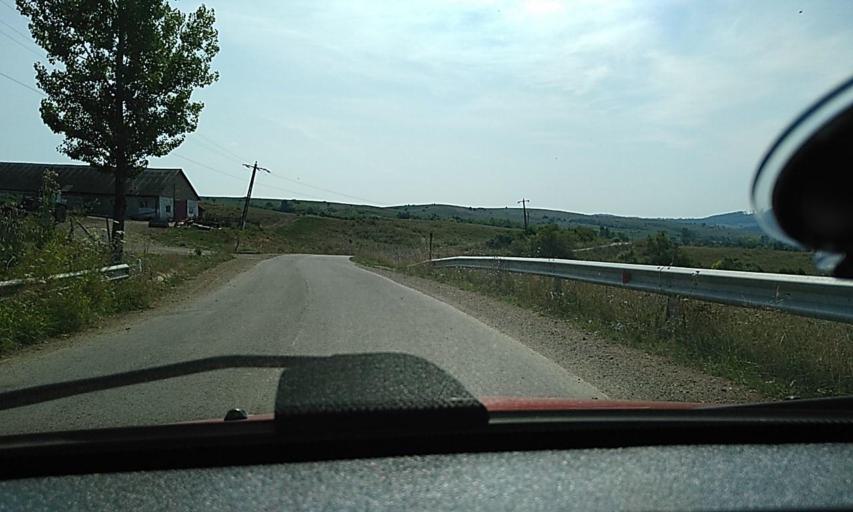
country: RO
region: Brasov
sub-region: Oras Rupea
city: Fiser
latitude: 46.0317
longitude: 25.1403
